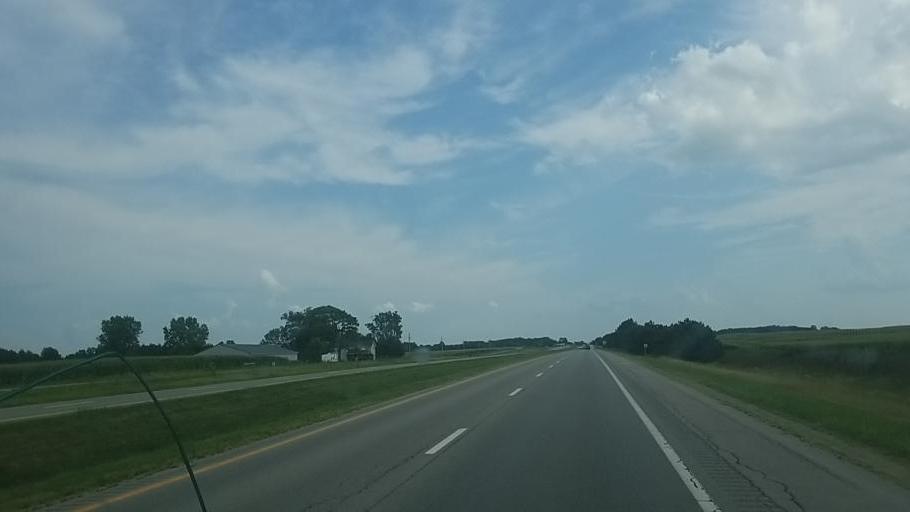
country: US
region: Ohio
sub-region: Wyandot County
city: Upper Sandusky
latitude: 40.7655
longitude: -83.2375
